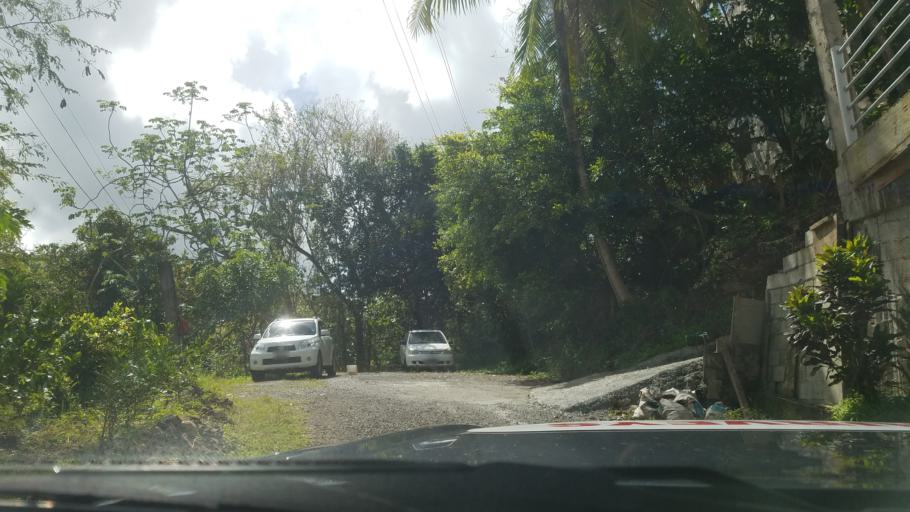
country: LC
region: Castries Quarter
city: Bisee
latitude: 14.0156
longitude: -60.9807
